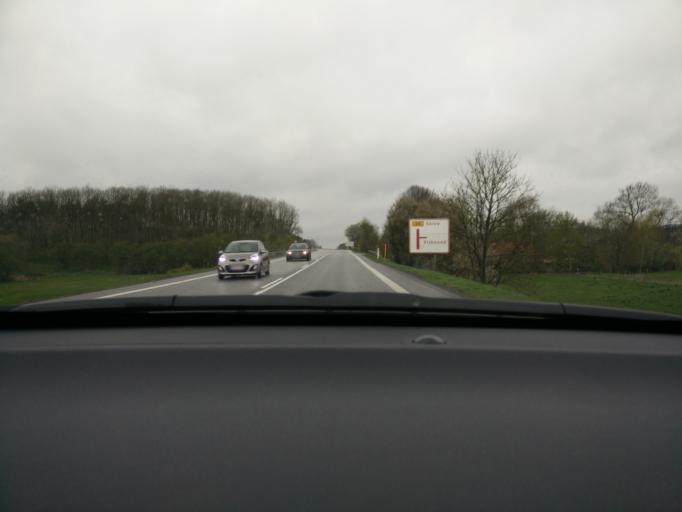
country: DK
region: Central Jutland
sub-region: Viborg Kommune
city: Viborg
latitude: 56.5136
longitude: 9.3004
